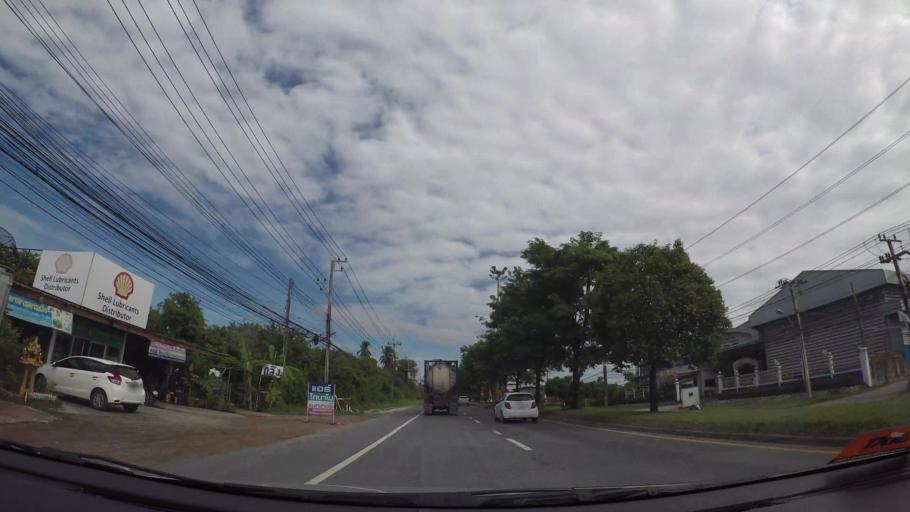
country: TH
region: Rayong
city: Ban Chang
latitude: 12.7362
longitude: 101.1290
